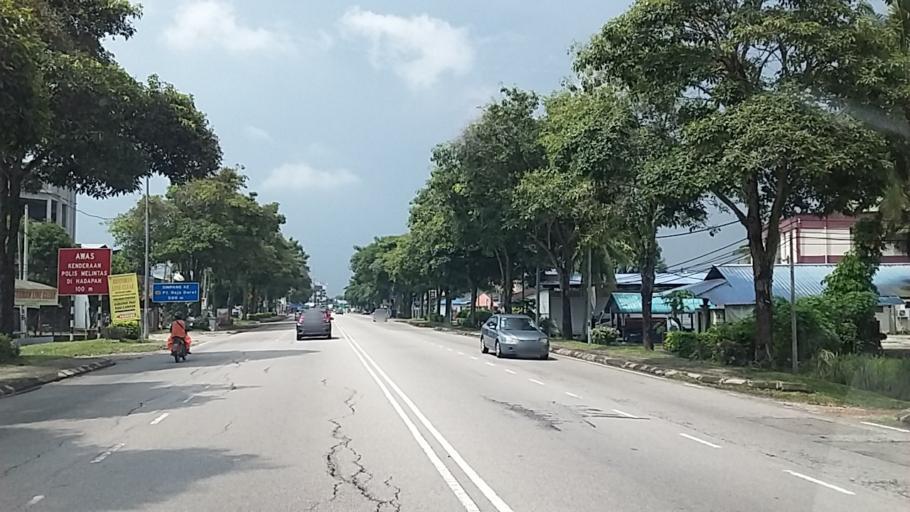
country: MY
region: Johor
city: Parit Raja
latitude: 1.8629
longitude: 103.1077
